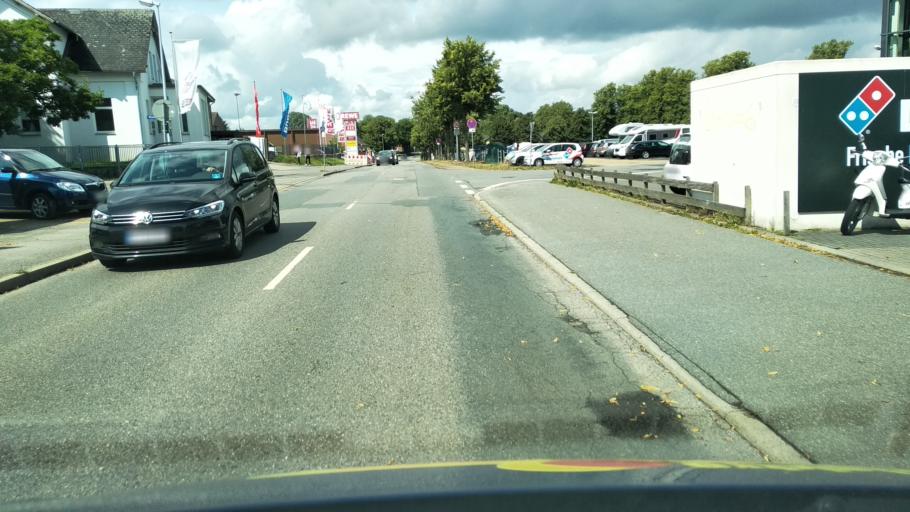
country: DE
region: Schleswig-Holstein
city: Schleswig
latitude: 54.5211
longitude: 9.5639
